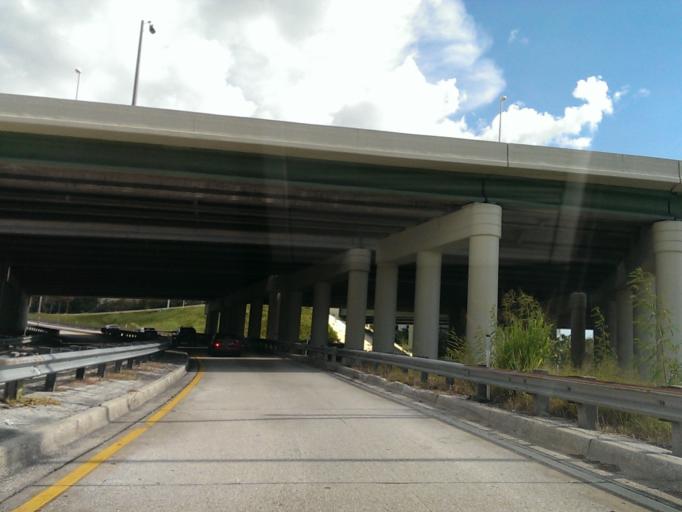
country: US
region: Florida
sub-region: Hillsborough County
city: Tampa
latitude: 27.9570
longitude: -82.4636
